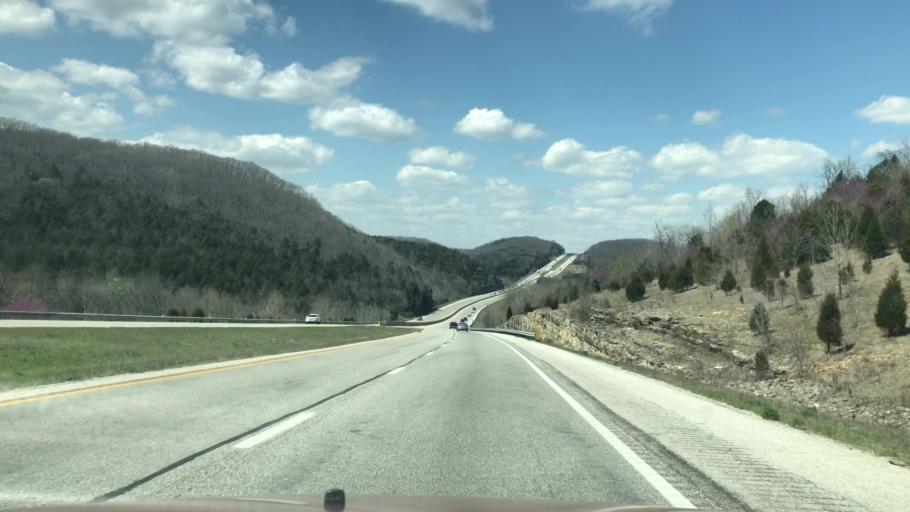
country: US
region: Missouri
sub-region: Taney County
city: Merriam Woods
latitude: 36.8542
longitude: -93.2240
